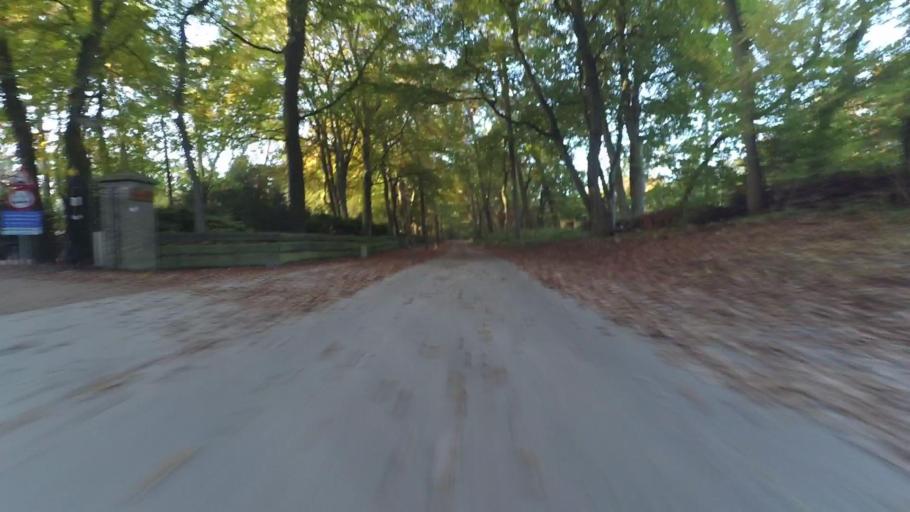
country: NL
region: Utrecht
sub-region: Gemeente Baarn
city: Baarn
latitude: 52.1953
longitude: 5.2456
